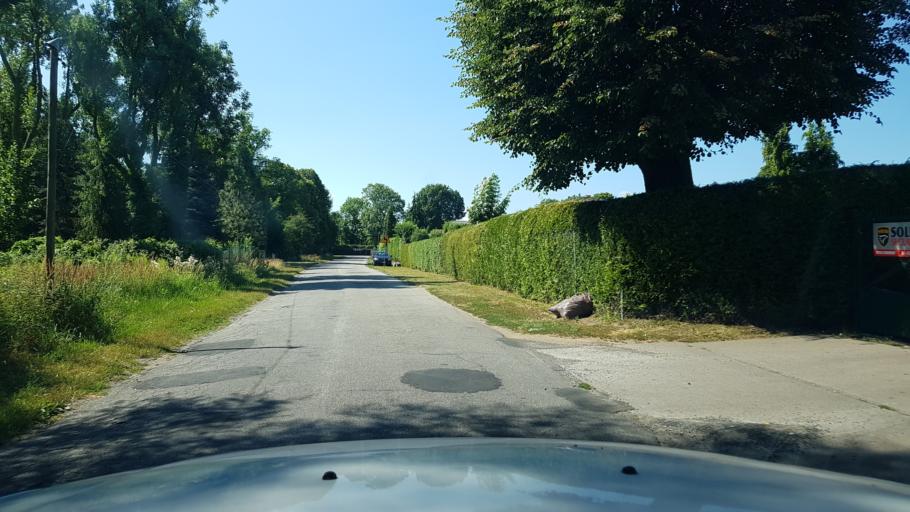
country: PL
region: West Pomeranian Voivodeship
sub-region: Powiat goleniowski
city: Goleniow
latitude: 53.4629
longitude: 14.7139
